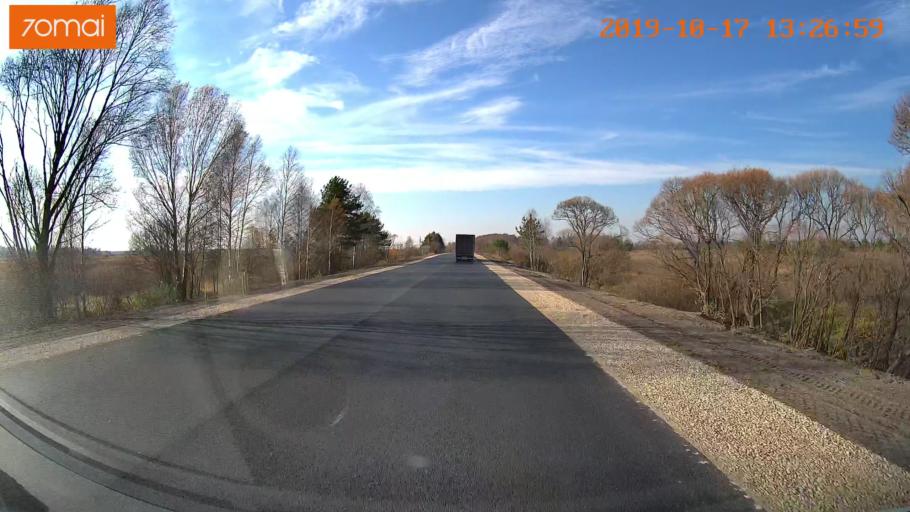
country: RU
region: Rjazan
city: Gus'-Zheleznyy
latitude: 55.1118
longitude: 40.9059
